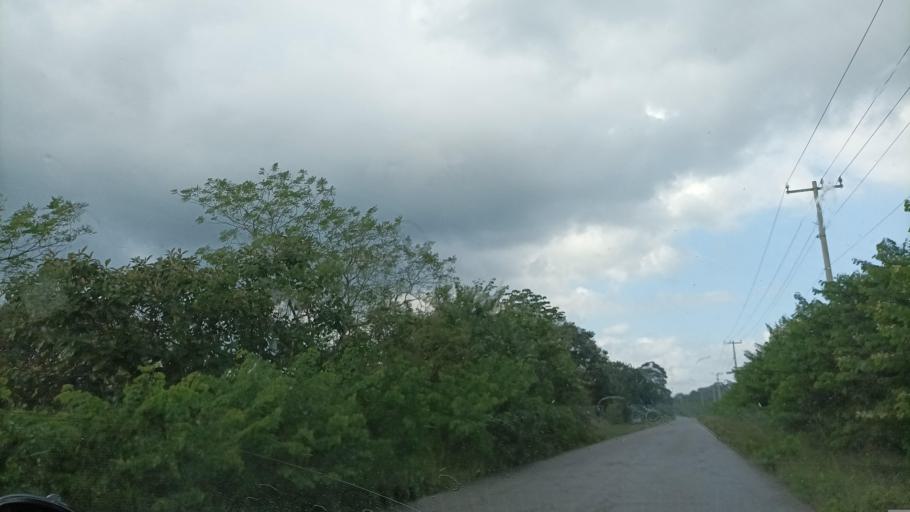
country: MX
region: Veracruz
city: Las Choapas
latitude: 17.8435
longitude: -94.1044
